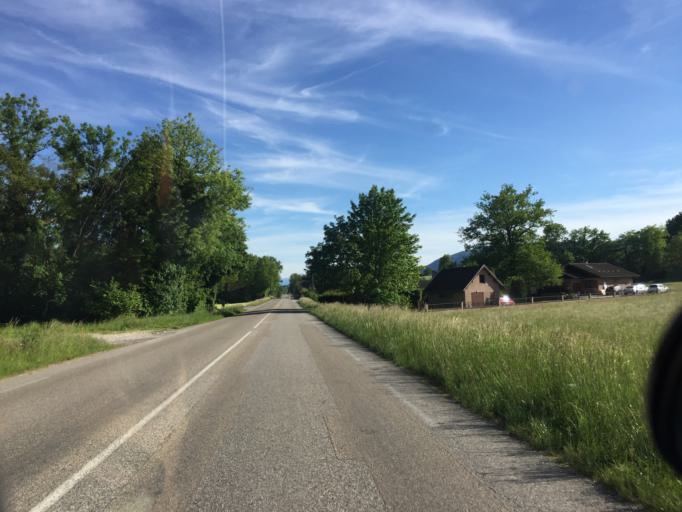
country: FR
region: Rhone-Alpes
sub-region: Departement de la Haute-Savoie
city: Saint-Felix
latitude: 45.8056
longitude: 5.9503
